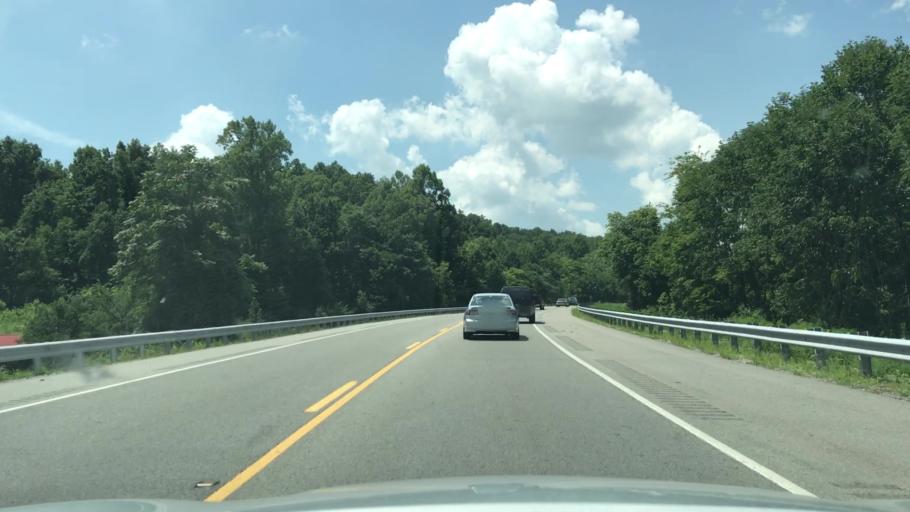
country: US
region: Tennessee
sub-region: Overton County
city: Livingston
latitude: 36.4034
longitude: -85.2922
